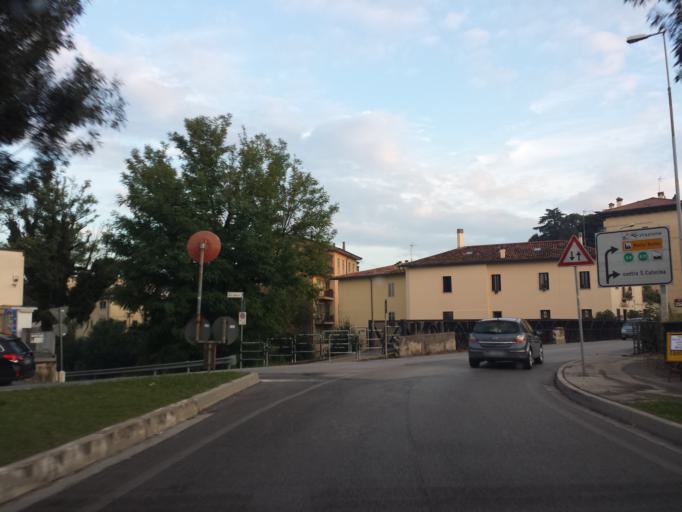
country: IT
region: Veneto
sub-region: Provincia di Vicenza
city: Vicenza
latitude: 45.5425
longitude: 11.5529
